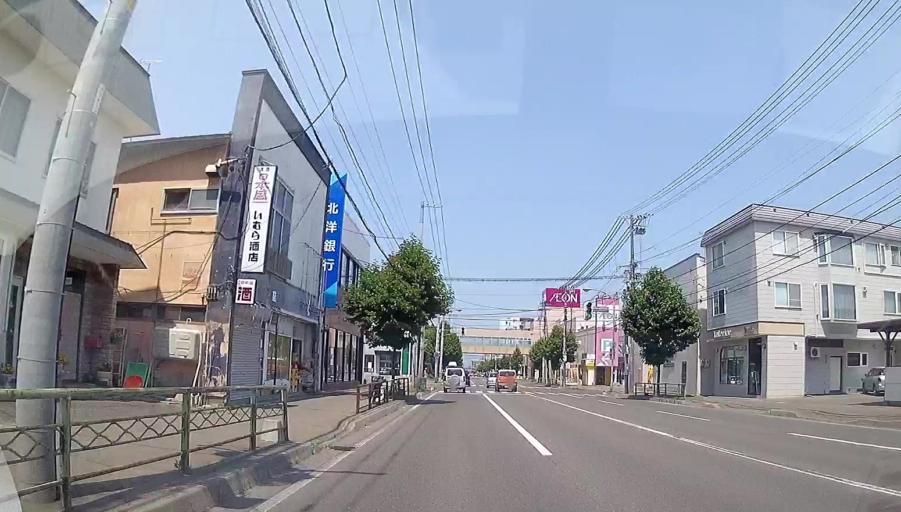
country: JP
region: Hokkaido
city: Obihiro
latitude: 42.9077
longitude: 143.1992
